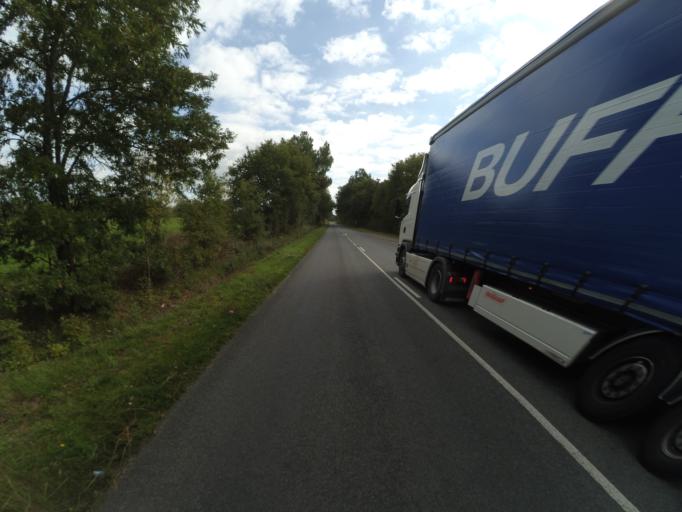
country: FR
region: Pays de la Loire
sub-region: Departement de la Loire-Atlantique
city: Bouvron
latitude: 47.4587
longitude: -1.8289
